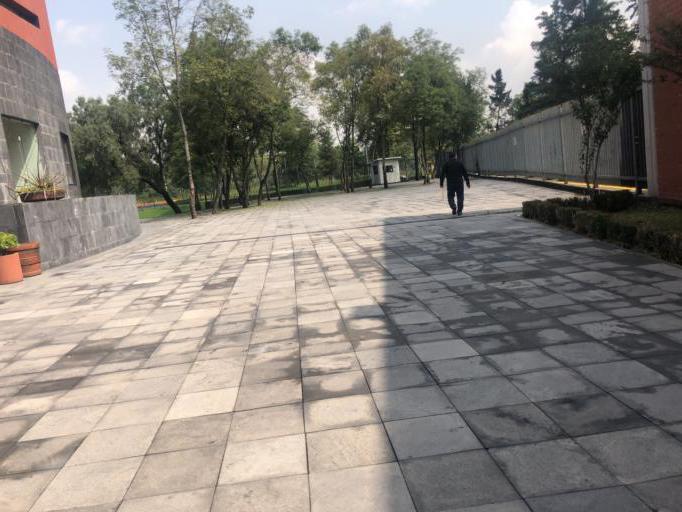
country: MX
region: Mexico City
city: Tlalpan
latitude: 19.3108
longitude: -99.1858
